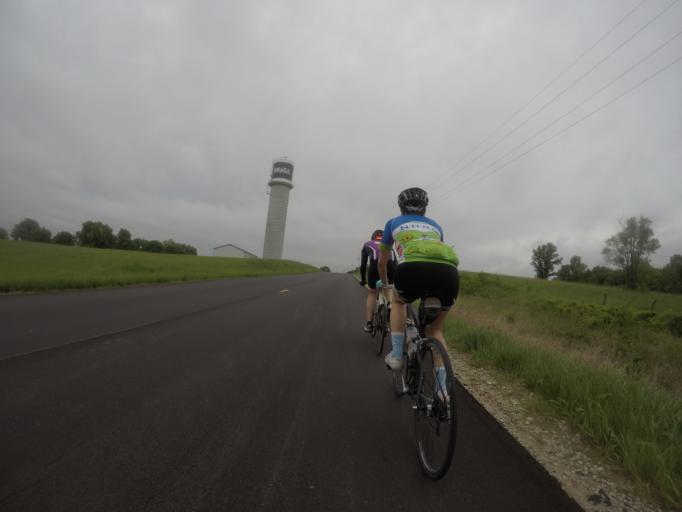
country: US
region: Kansas
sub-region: Pottawatomie County
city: Westmoreland
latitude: 39.5002
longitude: -96.1697
